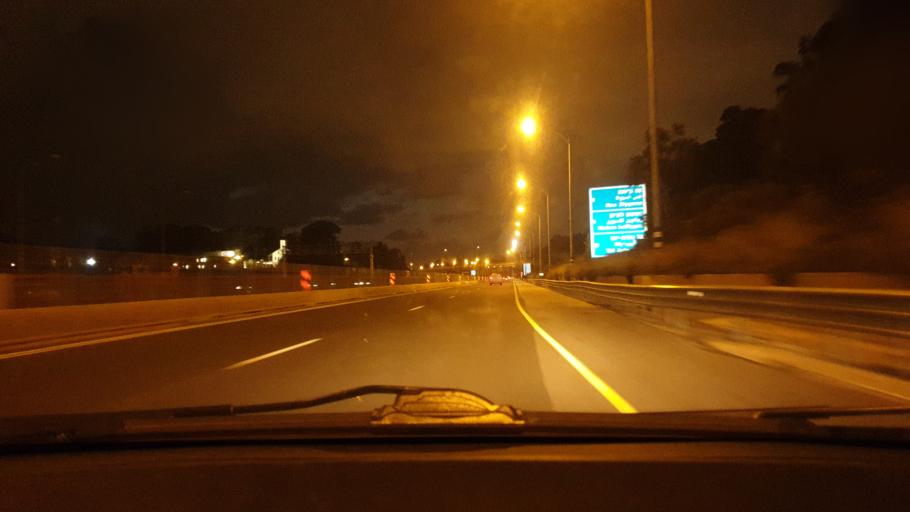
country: IL
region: Central District
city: Ramla
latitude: 31.9248
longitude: 34.8330
